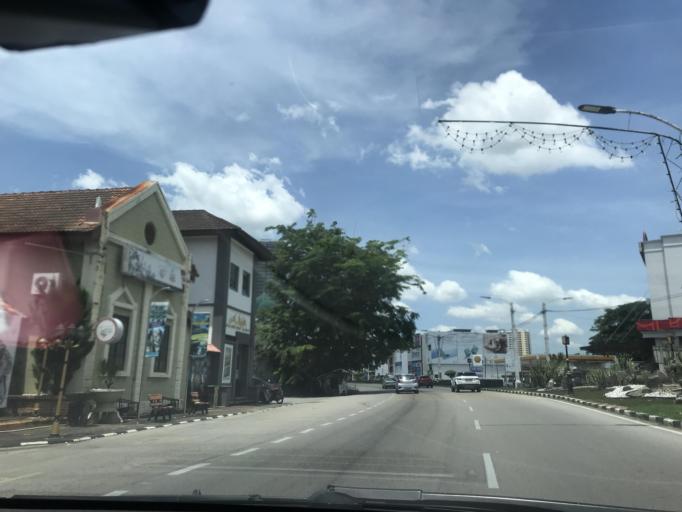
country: MY
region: Kelantan
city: Kota Bharu
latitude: 6.1244
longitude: 102.2381
